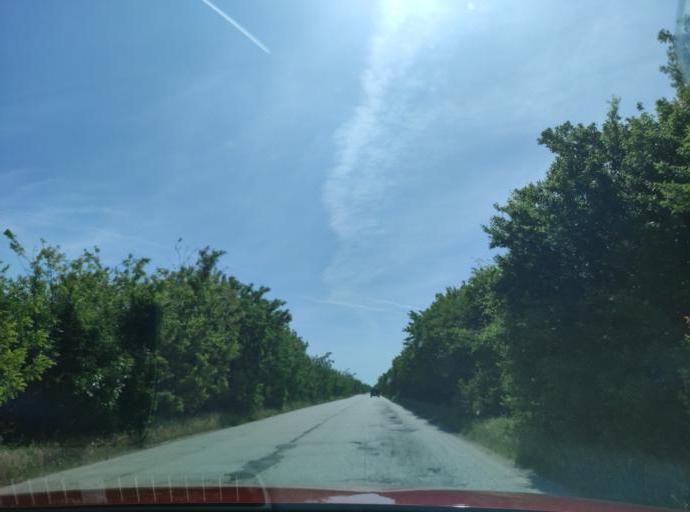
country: BG
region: Pleven
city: Iskur
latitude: 43.4506
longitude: 24.3138
